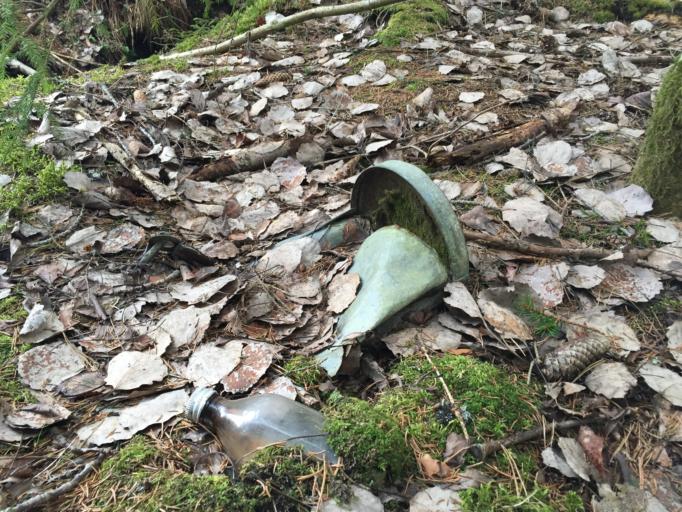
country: SE
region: Soedermanland
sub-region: Vingakers Kommun
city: Vingaker
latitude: 58.9730
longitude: 15.7051
